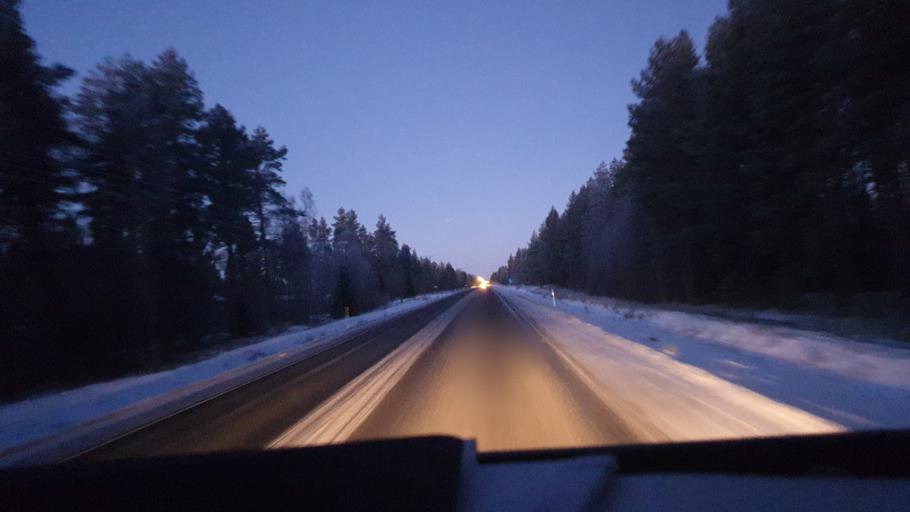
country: FI
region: Northern Ostrobothnia
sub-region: Raahe
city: Siikajoki
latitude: 64.6928
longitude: 24.6630
